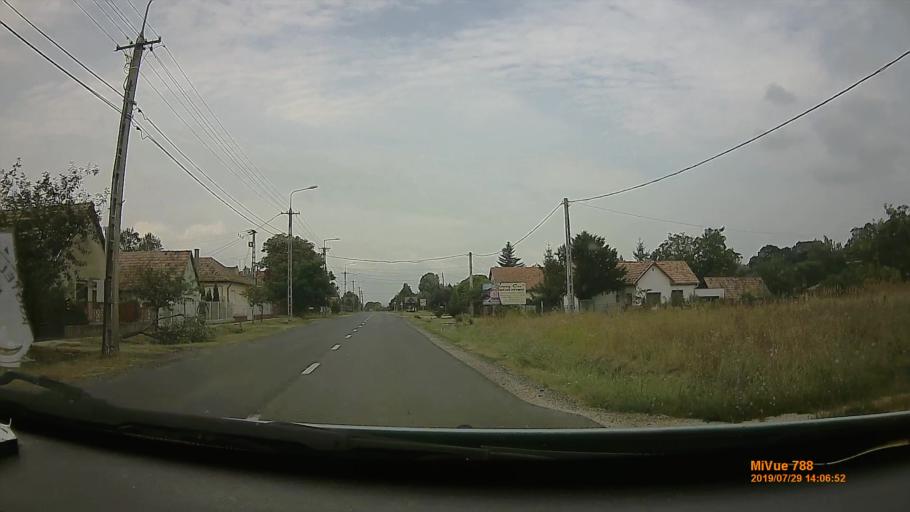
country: HU
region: Somogy
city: Balatonfoldvar
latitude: 46.8204
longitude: 17.9061
